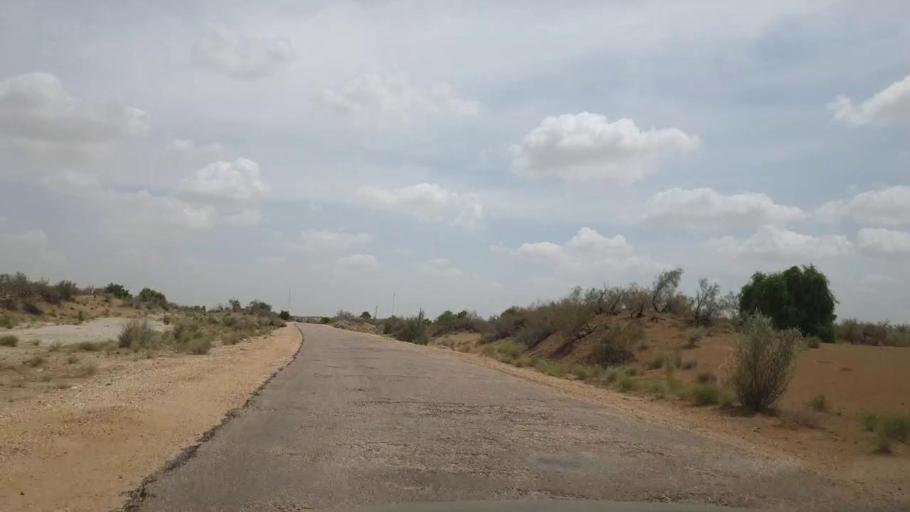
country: PK
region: Sindh
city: Kot Diji
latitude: 27.1430
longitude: 69.2245
